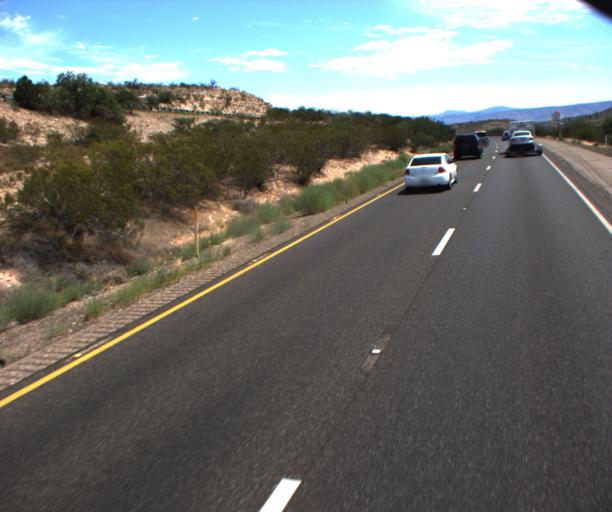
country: US
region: Arizona
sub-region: Yavapai County
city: Lake Montezuma
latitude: 34.6356
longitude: -111.8259
